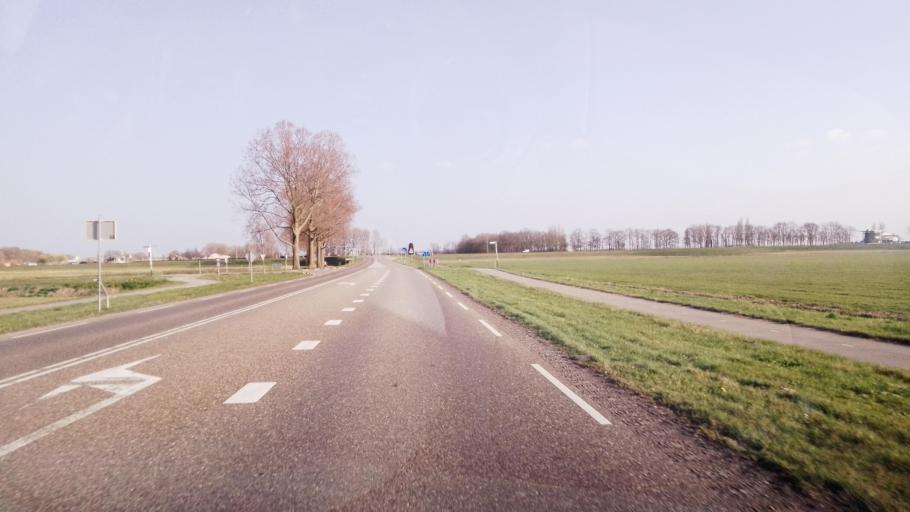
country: NL
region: Gelderland
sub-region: Gemeente Elburg
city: Elburg
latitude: 52.4609
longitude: 5.8088
